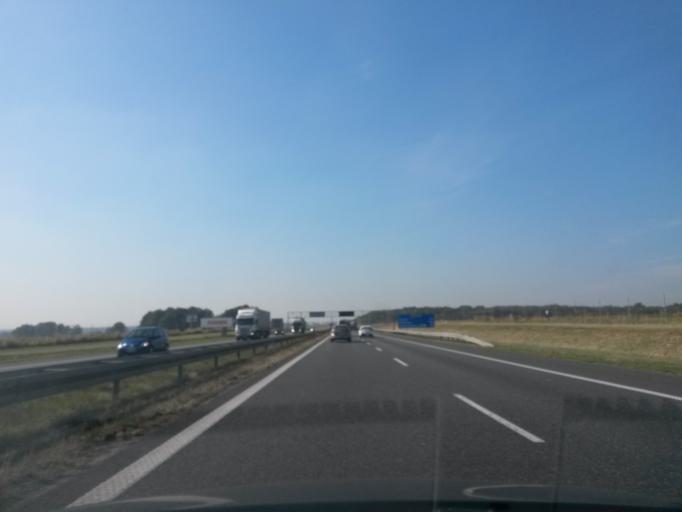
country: PL
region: Silesian Voivodeship
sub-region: Powiat gliwicki
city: Zernica
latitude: 50.2615
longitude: 18.6383
